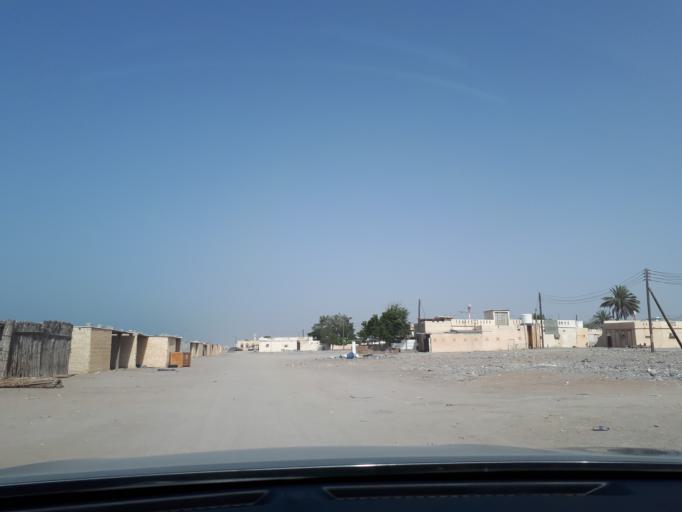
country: OM
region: Al Batinah
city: Barka'
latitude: 23.7077
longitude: 57.9276
